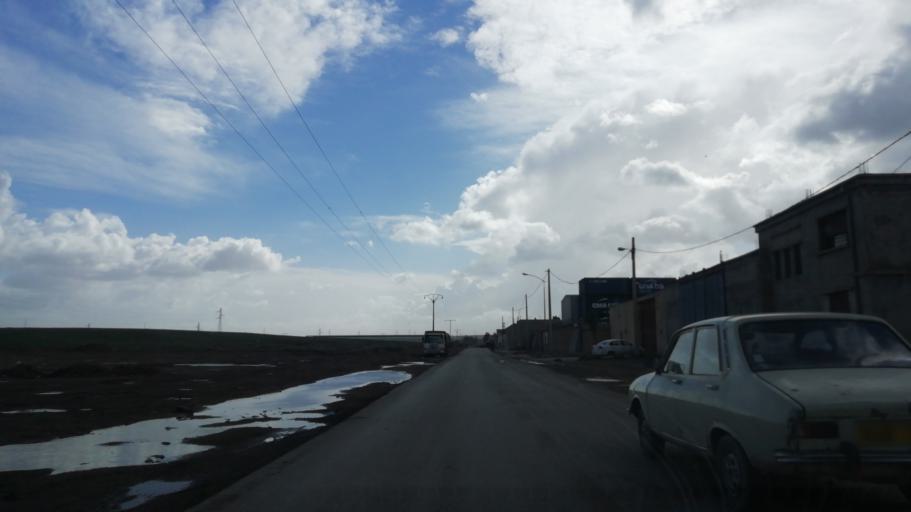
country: DZ
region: Oran
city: Sidi ech Chahmi
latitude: 35.6457
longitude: -0.5588
